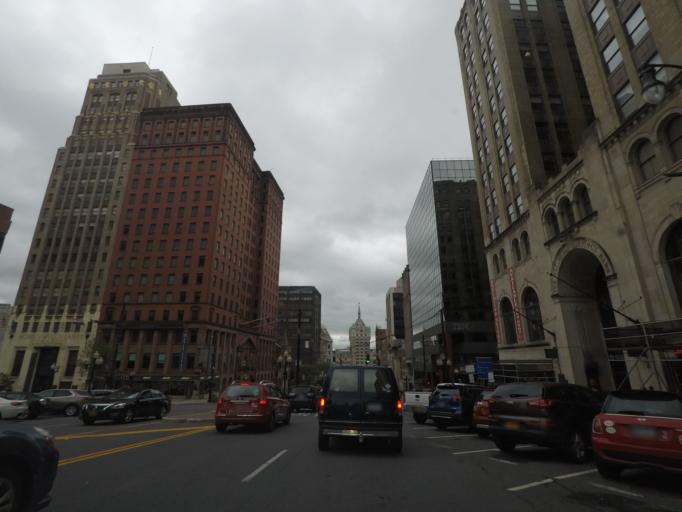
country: US
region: New York
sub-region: Albany County
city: Albany
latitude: 42.6500
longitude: -73.7533
